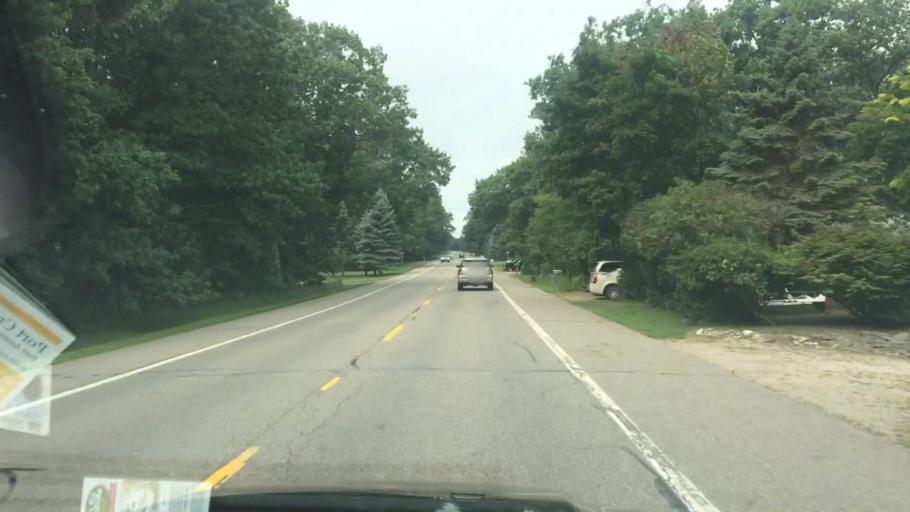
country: US
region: Michigan
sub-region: Huron County
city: Pigeon
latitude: 43.9801
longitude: -83.2241
